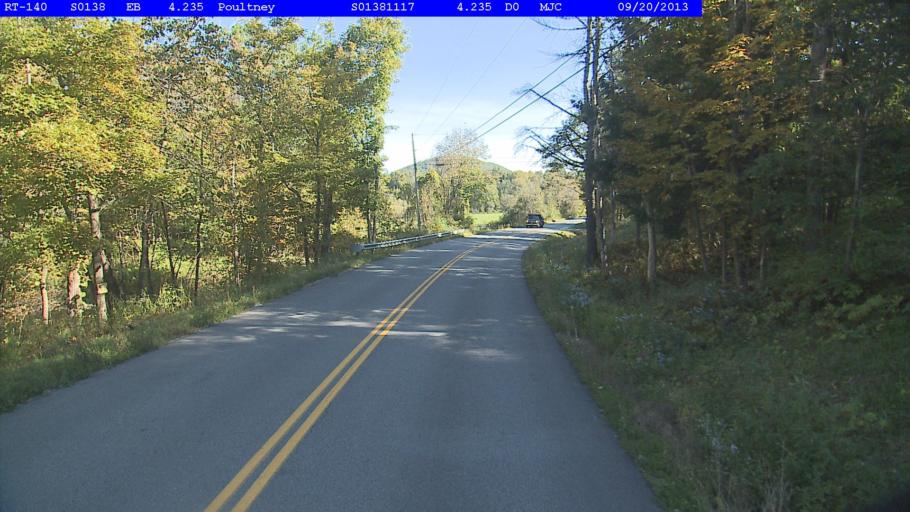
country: US
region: Vermont
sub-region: Rutland County
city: Poultney
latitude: 43.5052
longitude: -73.1764
